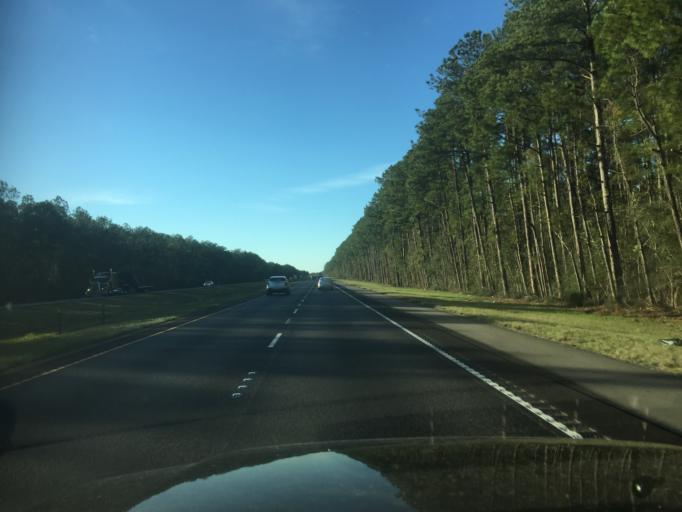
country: US
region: Louisiana
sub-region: Saint Tammany Parish
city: Lacombe
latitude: 30.3645
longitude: -89.9433
